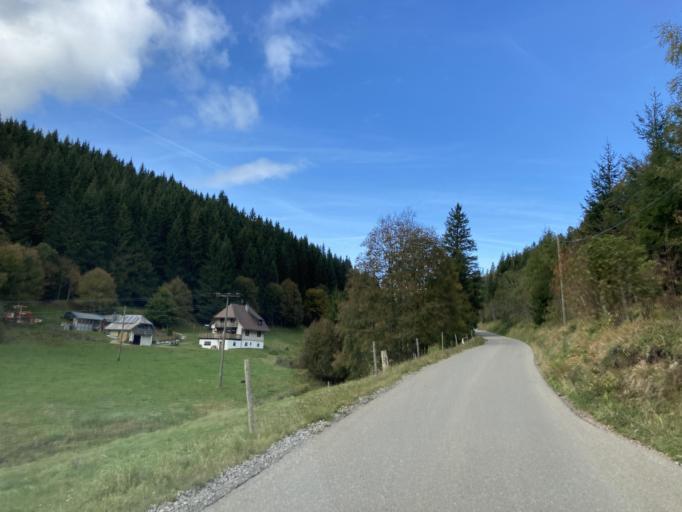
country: DE
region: Baden-Wuerttemberg
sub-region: Freiburg Region
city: Vohrenbach
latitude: 48.0599
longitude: 8.2858
